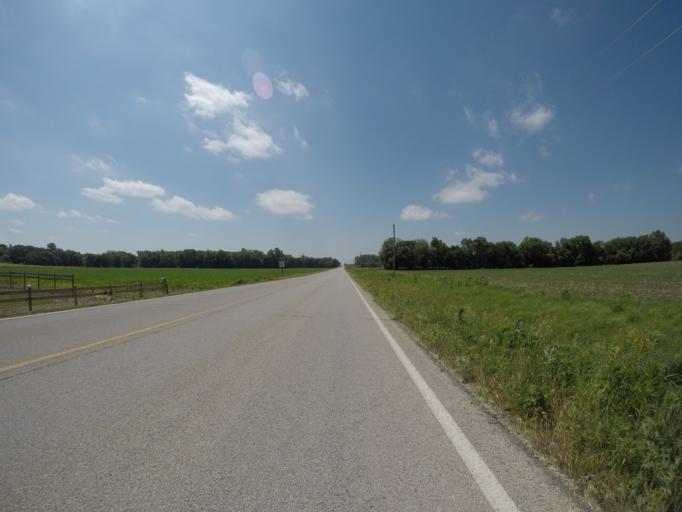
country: US
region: Kansas
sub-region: Pottawatomie County
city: Westmoreland
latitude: 39.3461
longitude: -96.4360
